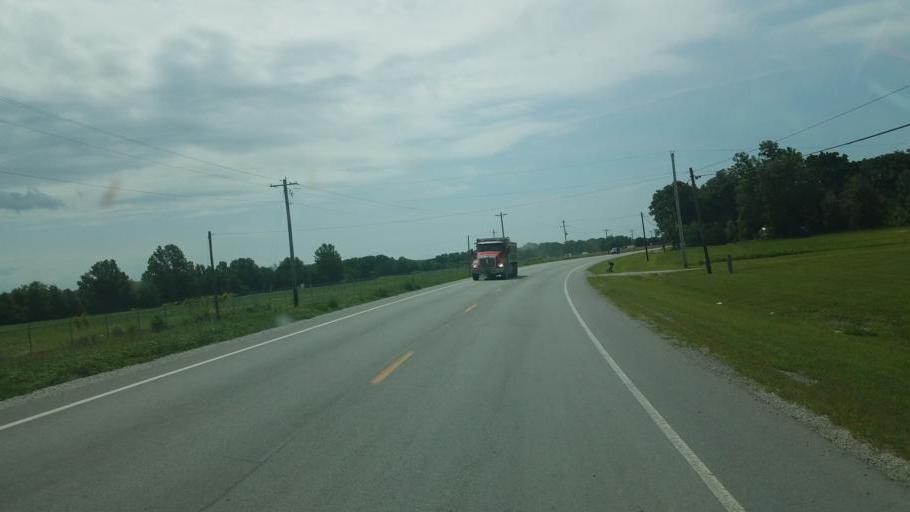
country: US
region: Ohio
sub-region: Wyandot County
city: Carey
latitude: 40.9073
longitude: -83.3353
